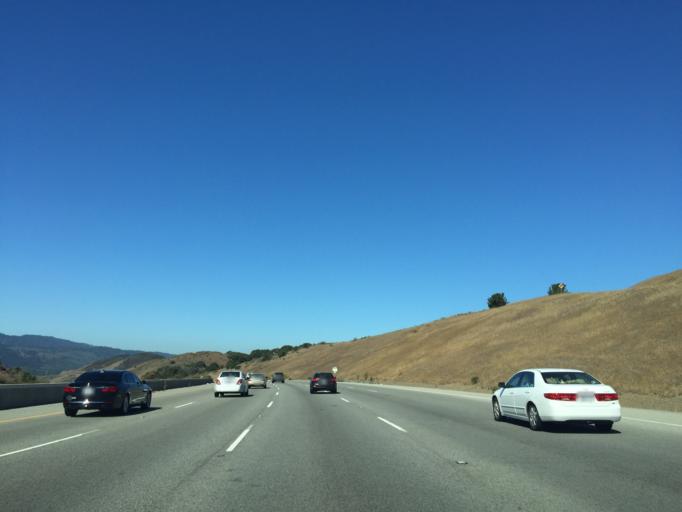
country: US
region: California
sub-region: San Mateo County
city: Belmont
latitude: 37.4927
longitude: -122.3011
